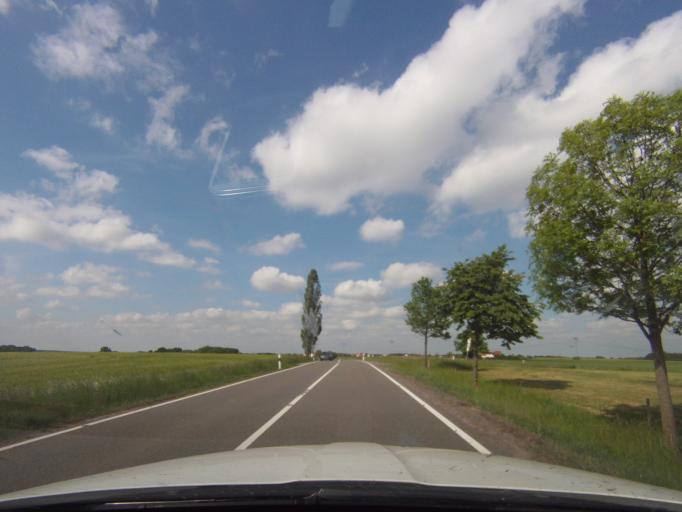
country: DE
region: Thuringia
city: Zedlitz
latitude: 50.8417
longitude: 12.0259
